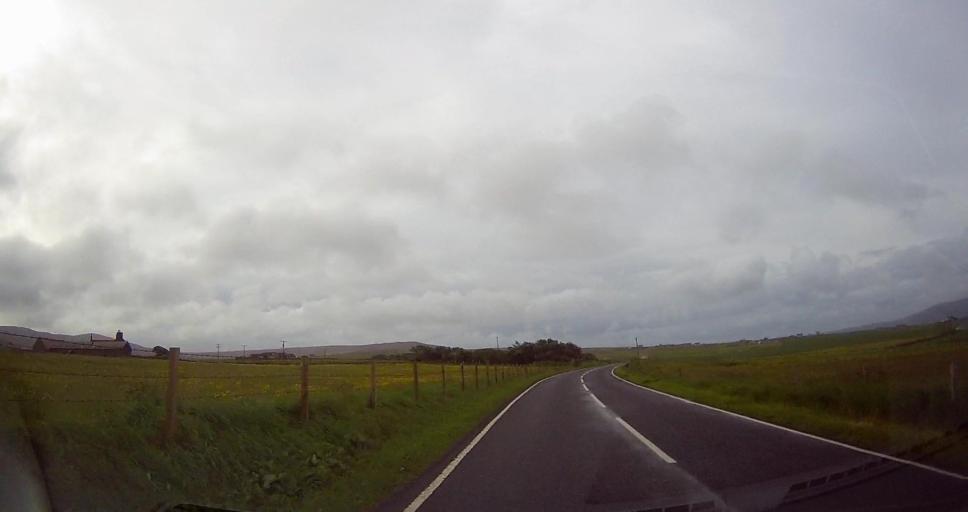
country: GB
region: Scotland
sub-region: Orkney Islands
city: Stromness
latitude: 58.9676
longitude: -3.2268
